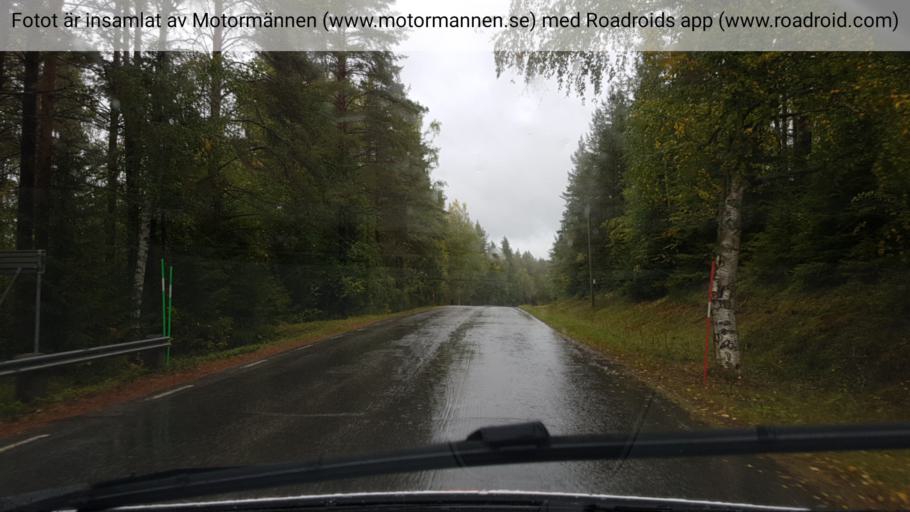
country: SE
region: Vaesterbotten
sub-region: Vannas Kommun
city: Vannasby
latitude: 64.1037
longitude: 19.9586
